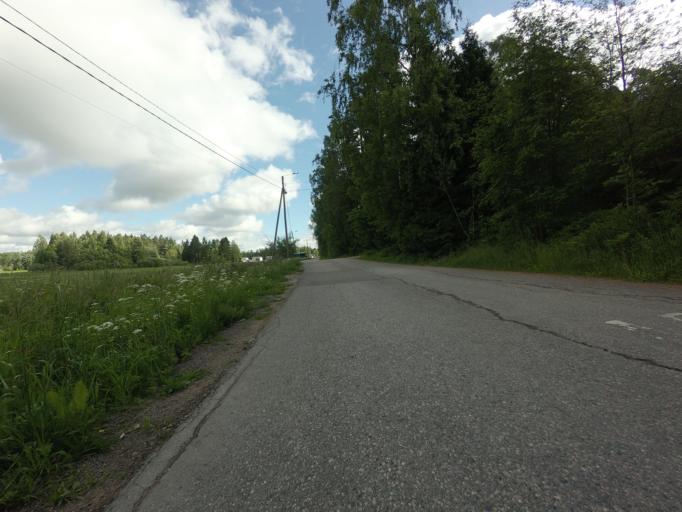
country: FI
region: Uusimaa
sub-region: Helsinki
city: Espoo
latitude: 60.1674
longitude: 24.5988
